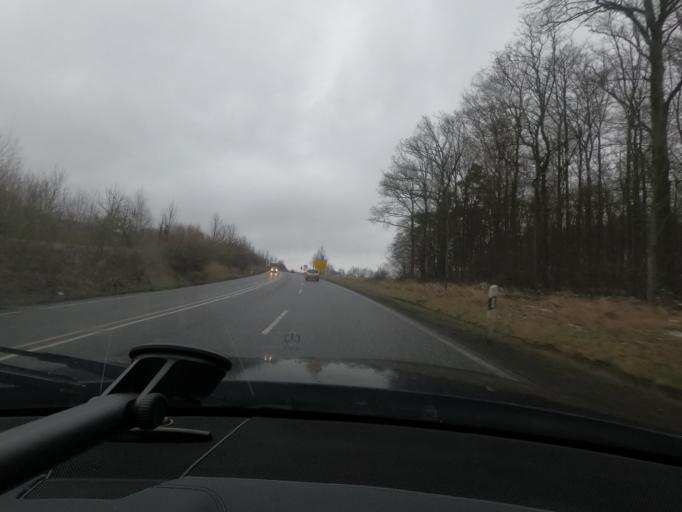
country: DE
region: Hesse
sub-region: Regierungsbezirk Kassel
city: Martinhagen
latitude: 51.3171
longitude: 9.2785
